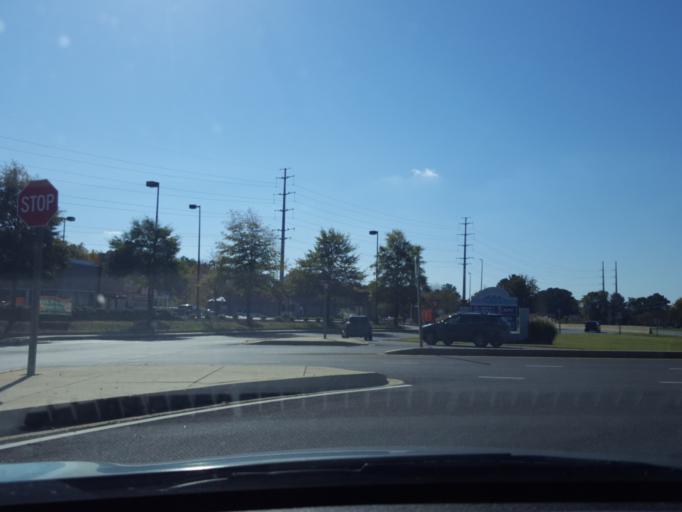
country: US
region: Maryland
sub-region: Calvert County
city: Solomons
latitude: 38.3469
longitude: -76.4606
